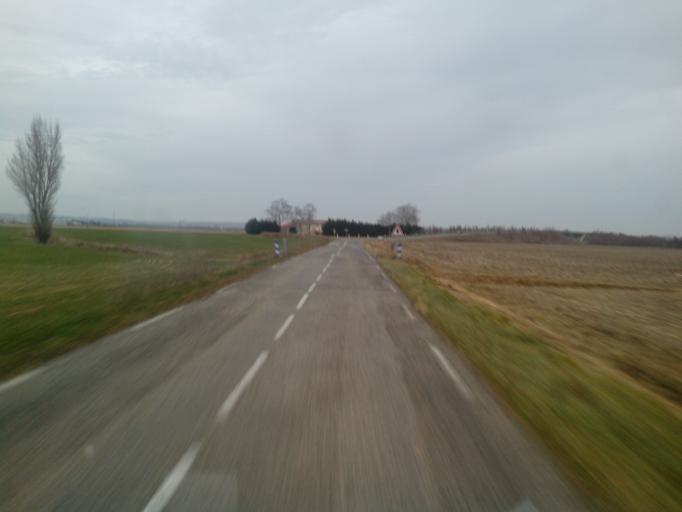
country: FR
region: Midi-Pyrenees
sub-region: Departement de l'Ariege
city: Mazeres
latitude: 43.2160
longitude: 1.6331
